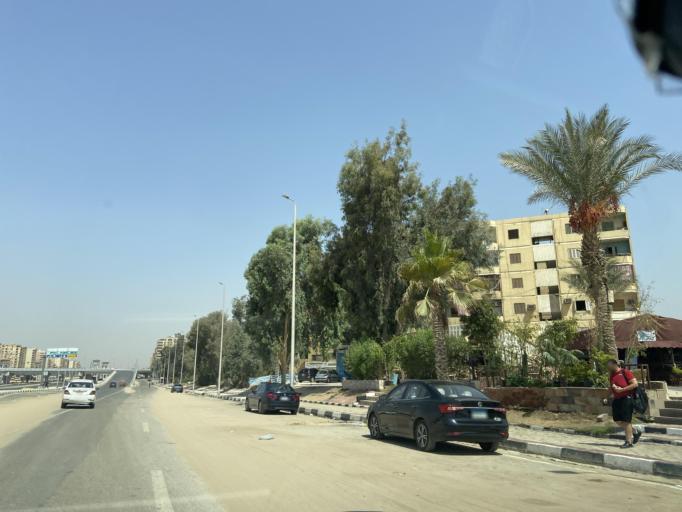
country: EG
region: Muhafazat al Qahirah
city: Cairo
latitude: 30.0439
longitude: 31.3631
